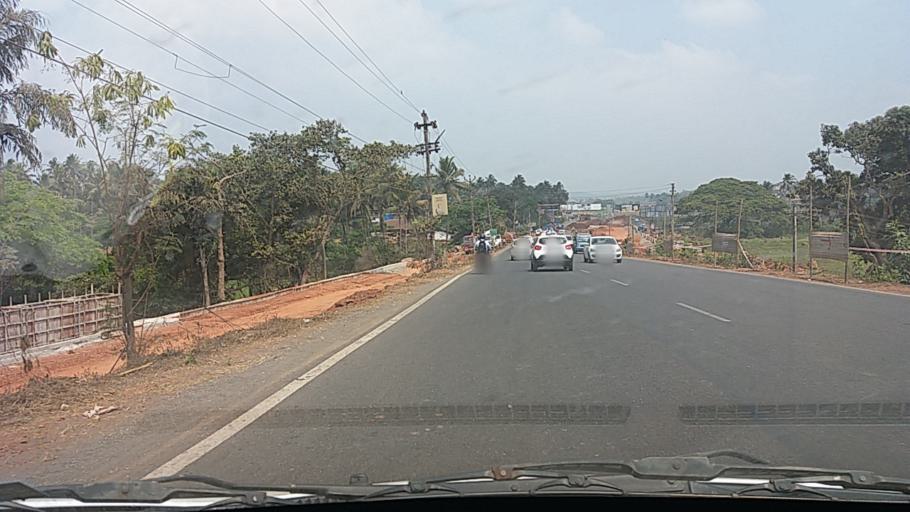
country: IN
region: Goa
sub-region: North Goa
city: Bambolim
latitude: 15.4695
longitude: 73.8507
